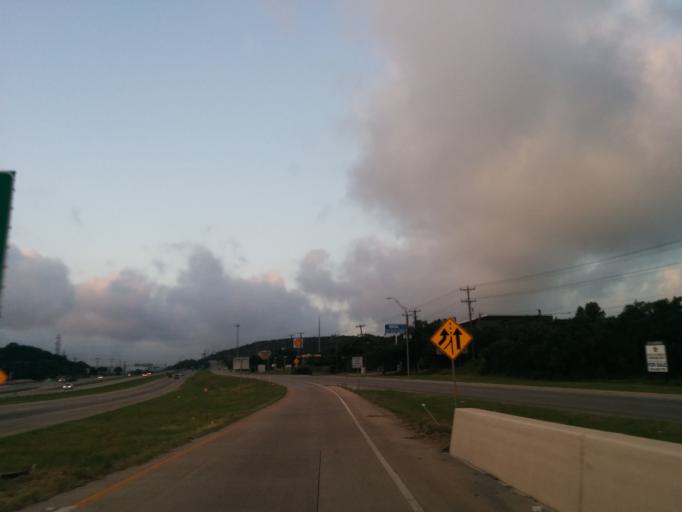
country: US
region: Texas
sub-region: Bexar County
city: Cross Mountain
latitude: 29.6235
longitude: -98.6096
